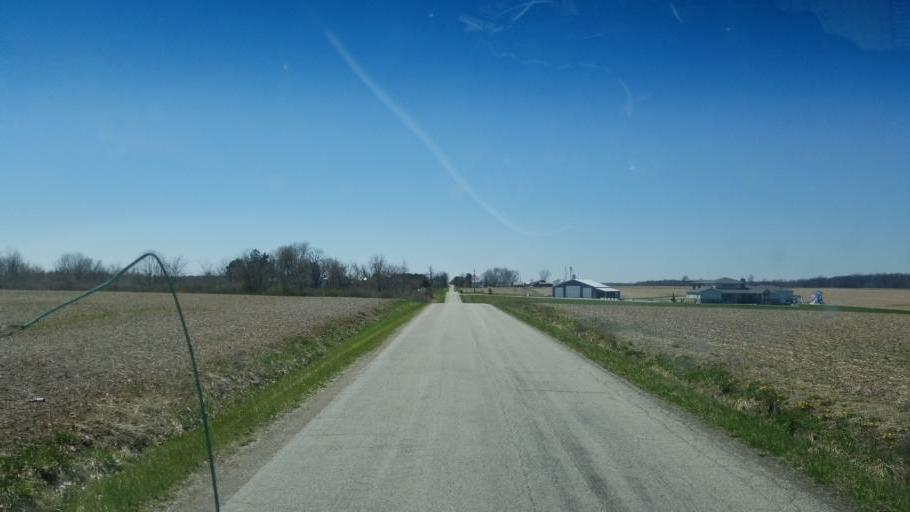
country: US
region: Ohio
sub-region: Huron County
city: Willard
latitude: 41.0806
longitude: -82.8331
